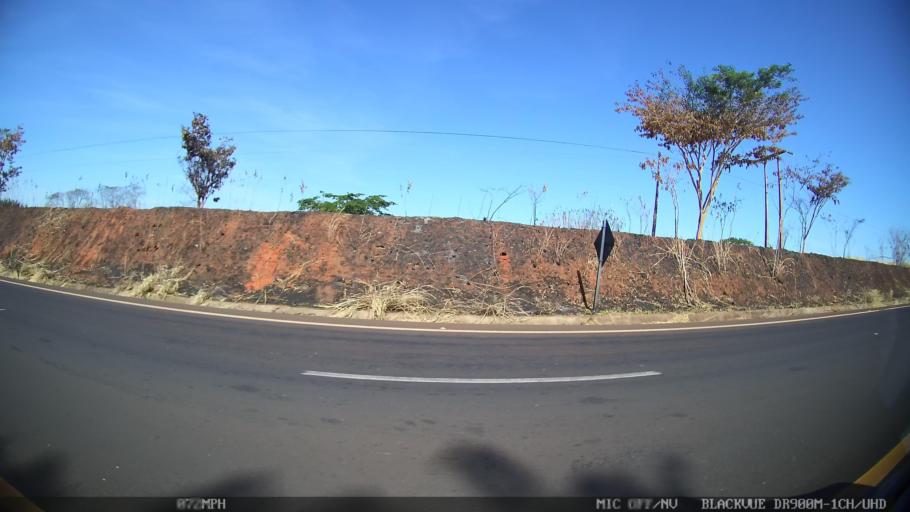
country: BR
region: Sao Paulo
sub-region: Barretos
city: Barretos
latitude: -20.5994
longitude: -48.7242
